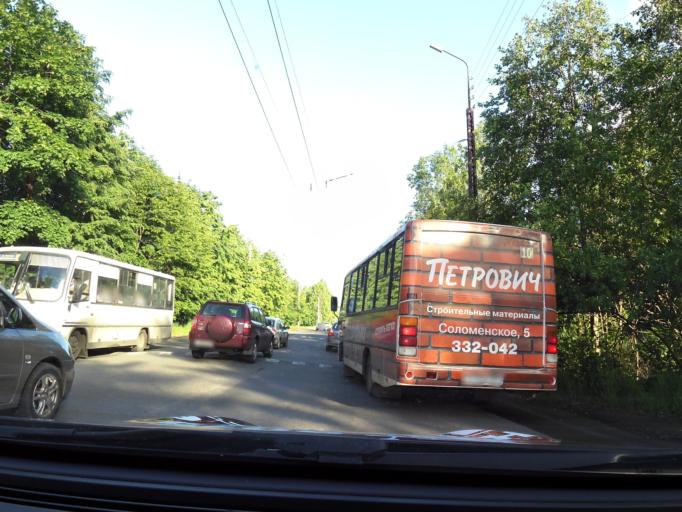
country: RU
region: Republic of Karelia
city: Petrozavodsk
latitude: 61.7622
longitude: 34.4197
